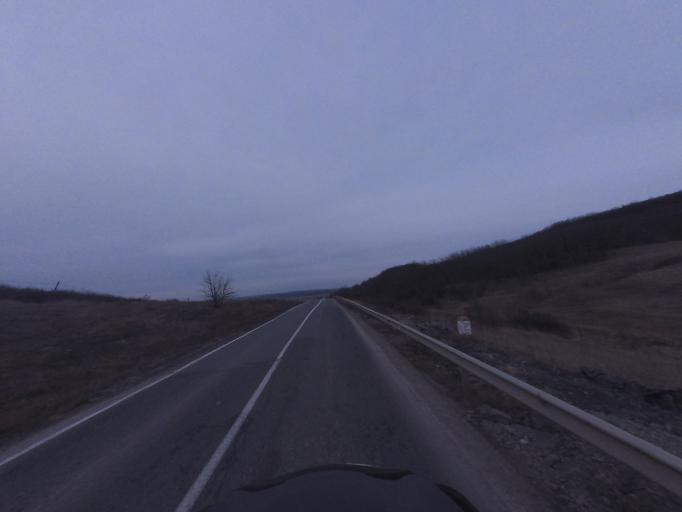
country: RO
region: Iasi
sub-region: Comuna Popricani
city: Popricani
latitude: 47.2974
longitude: 27.5100
